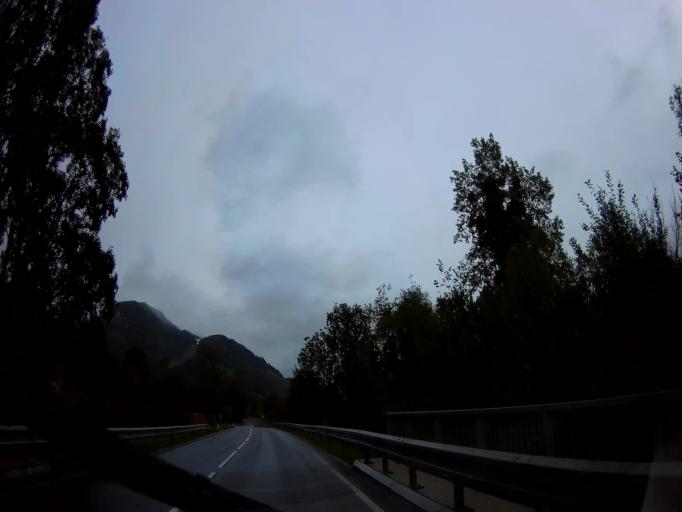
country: AT
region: Styria
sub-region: Politischer Bezirk Liezen
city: Weissenbach bei Liezen
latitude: 47.5654
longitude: 14.1952
